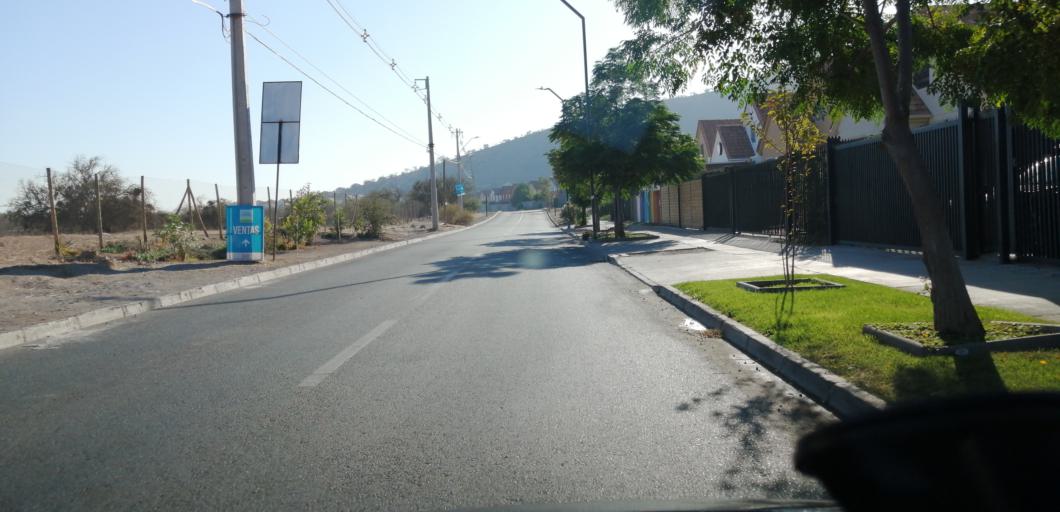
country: CL
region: Santiago Metropolitan
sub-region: Provincia de Santiago
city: Lo Prado
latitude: -33.4622
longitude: -70.8578
